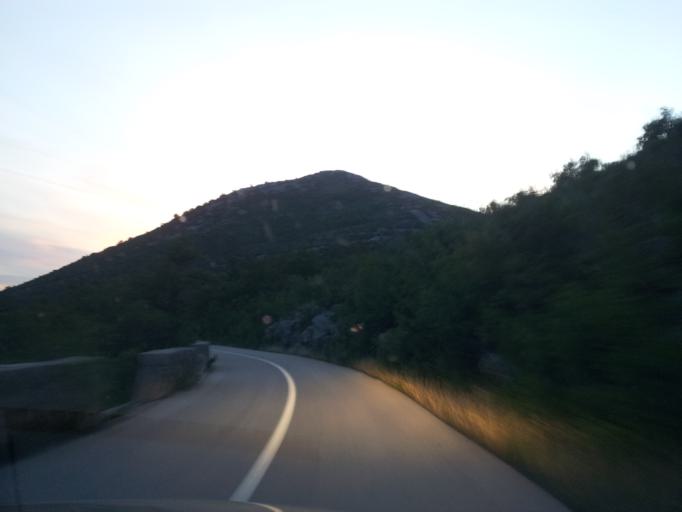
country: HR
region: Zadarska
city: Obrovac
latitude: 44.2381
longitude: 15.6686
